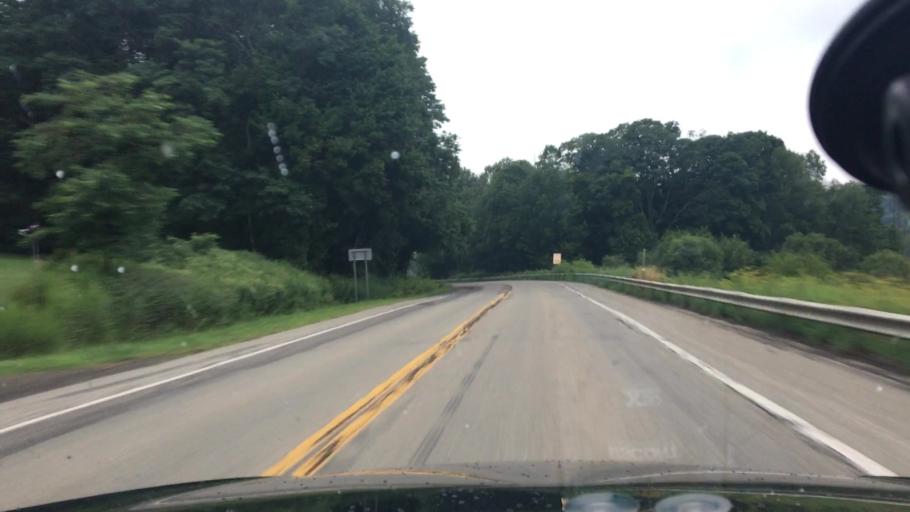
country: US
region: New York
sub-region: Cattaraugus County
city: Randolph
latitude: 42.1989
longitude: -78.8950
